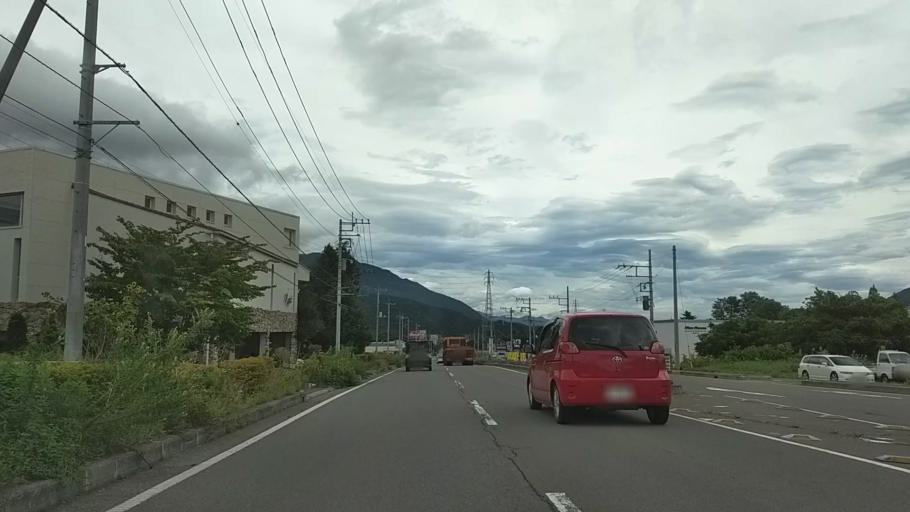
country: JP
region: Yamanashi
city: Fujikawaguchiko
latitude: 35.4860
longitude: 138.8119
